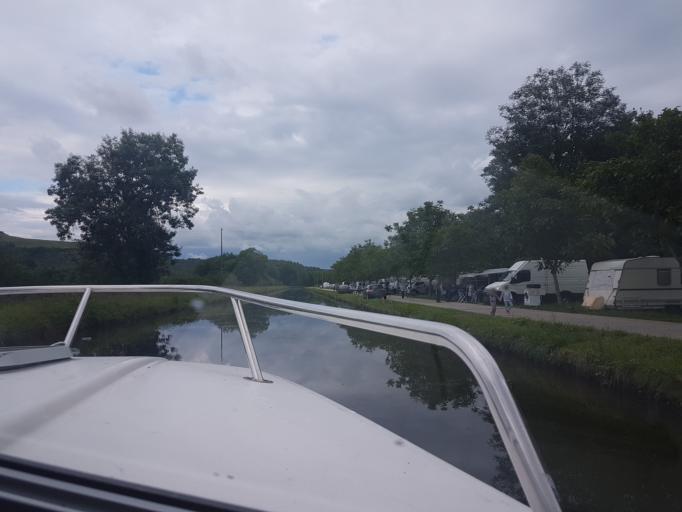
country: FR
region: Bourgogne
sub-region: Departement de l'Yonne
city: Saint-Bris-le-Vineux
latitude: 47.6963
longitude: 3.6475
